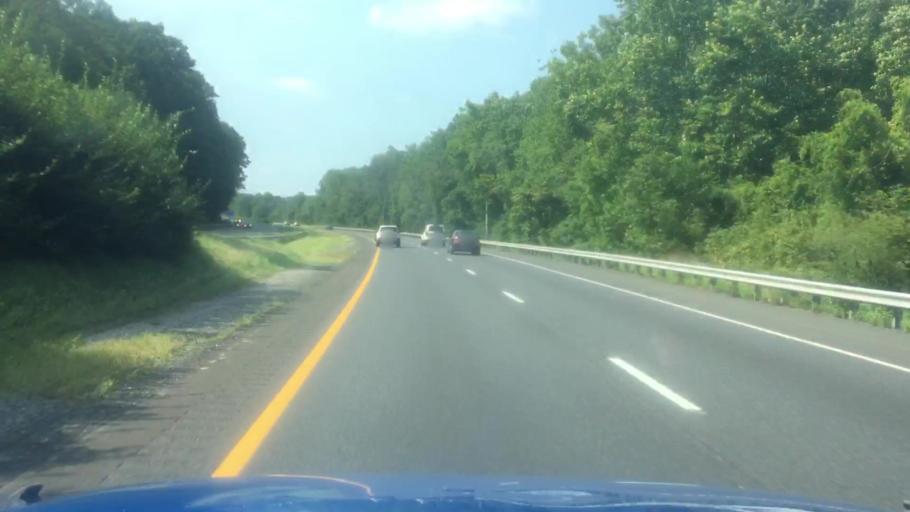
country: US
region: Maryland
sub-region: Baltimore County
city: Hunt Valley
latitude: 39.5641
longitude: -76.6656
